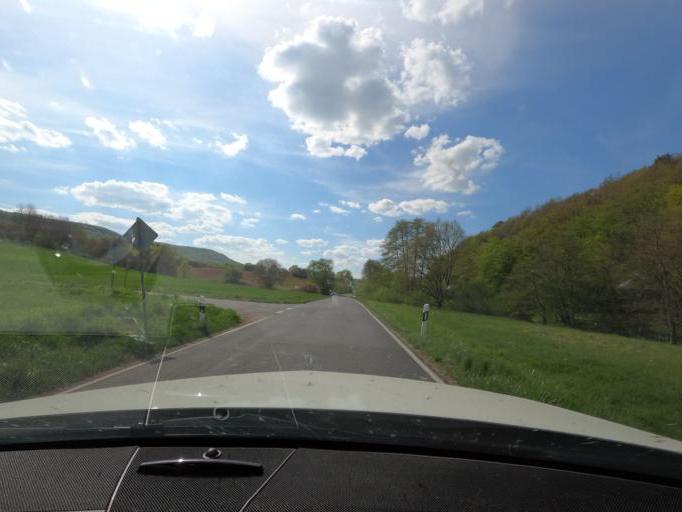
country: DE
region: Hesse
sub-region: Regierungsbezirk Kassel
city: Weissenborn
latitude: 51.1278
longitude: 10.1376
